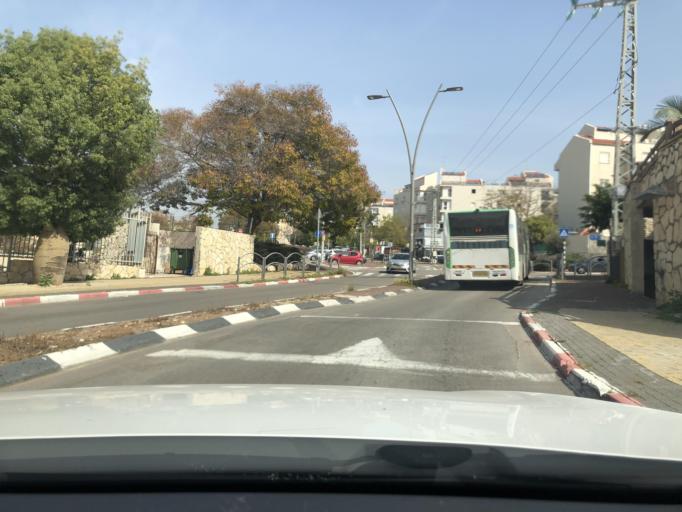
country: IL
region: Central District
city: Rosh Ha'Ayin
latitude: 32.0862
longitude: 34.9577
